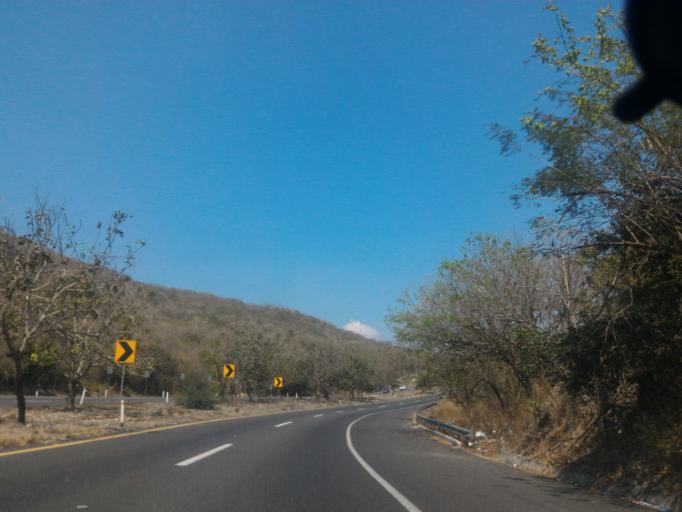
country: MX
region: Colima
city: Ixtlahuacan
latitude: 19.0310
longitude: -103.7946
